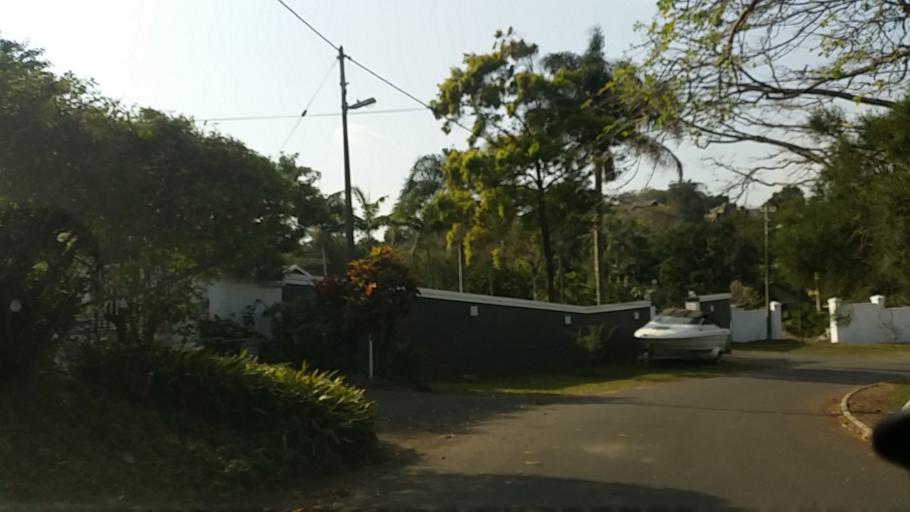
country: ZA
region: KwaZulu-Natal
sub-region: eThekwini Metropolitan Municipality
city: Berea
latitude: -29.8366
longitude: 30.9515
